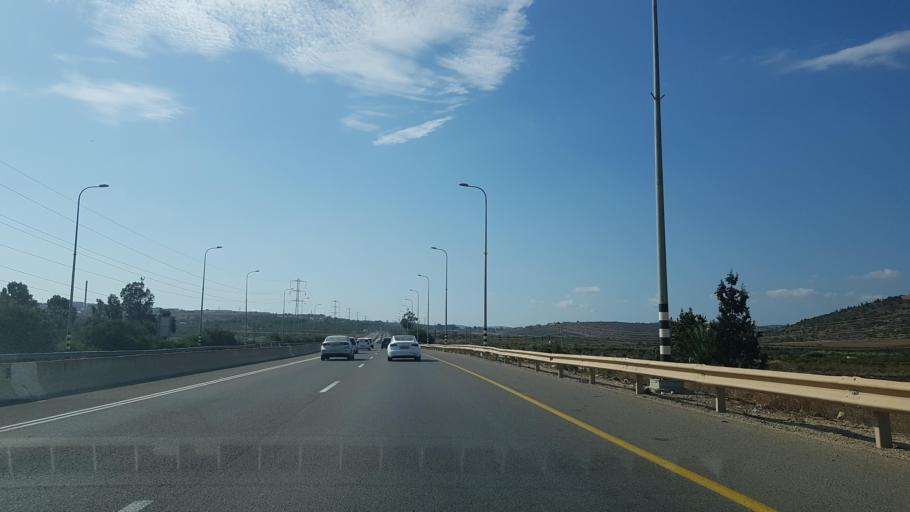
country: IL
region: Northern District
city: Kafr Kanna
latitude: 32.7628
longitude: 35.3403
